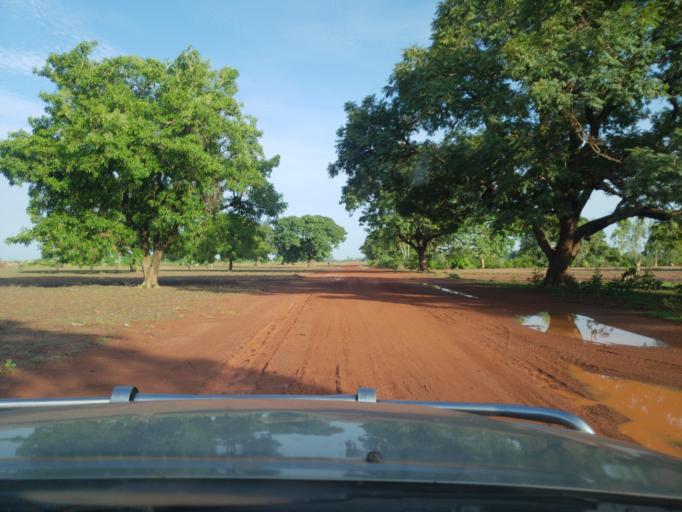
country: ML
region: Sikasso
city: Koutiala
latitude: 12.4281
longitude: -5.6024
